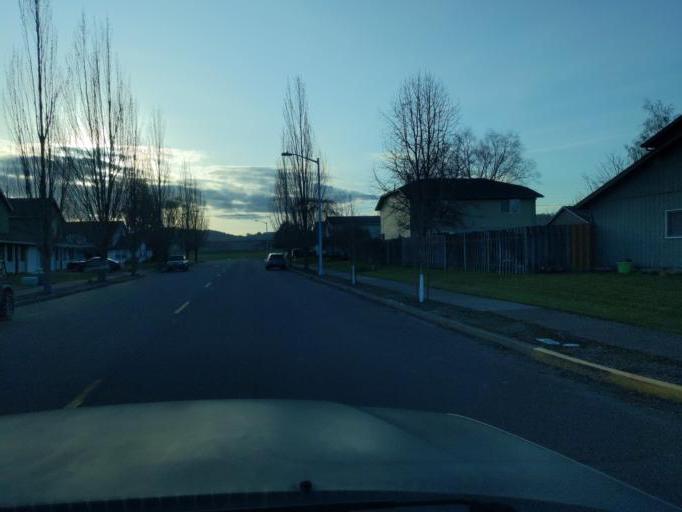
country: US
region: Oregon
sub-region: Yamhill County
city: McMinnville
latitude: 45.2022
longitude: -123.2281
